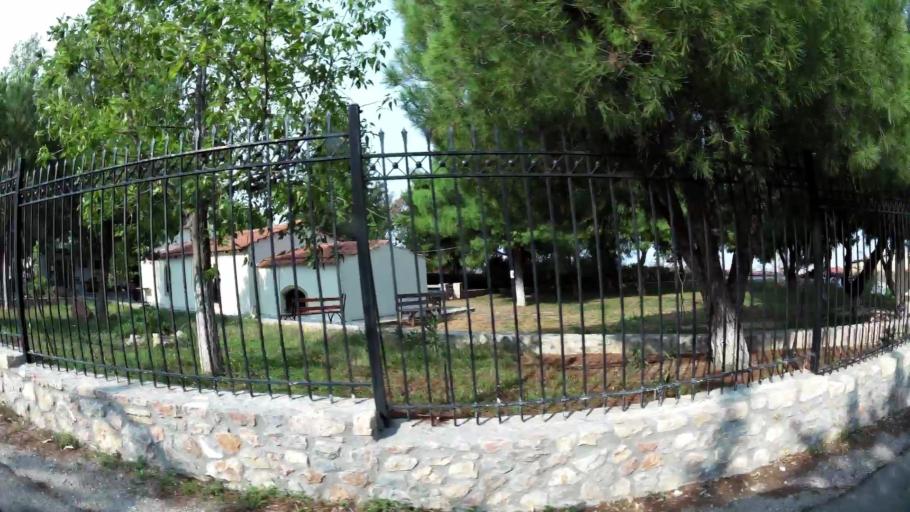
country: GR
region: Attica
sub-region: Nomarchia Athinas
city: Galatsi
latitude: 38.0042
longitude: 23.7553
